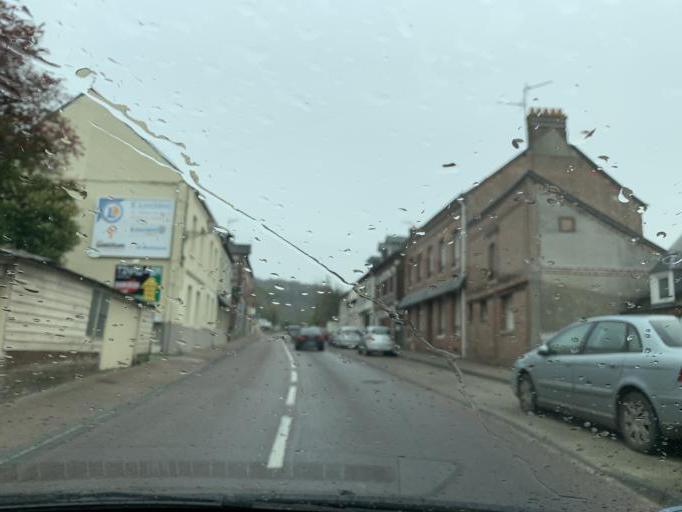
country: FR
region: Haute-Normandie
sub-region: Departement de la Seine-Maritime
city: Cany-Barville
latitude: 49.7874
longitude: 0.6401
